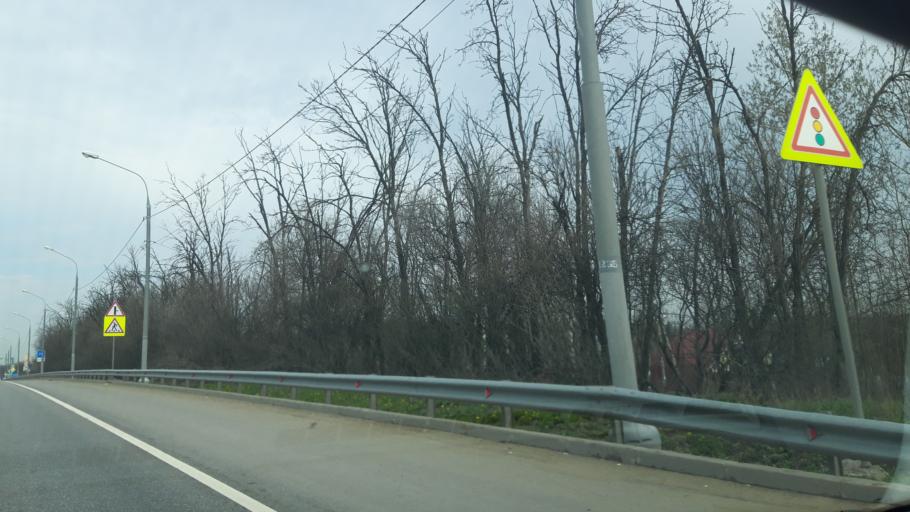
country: RU
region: Moskovskaya
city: Lozhki
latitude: 56.1114
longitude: 37.0896
